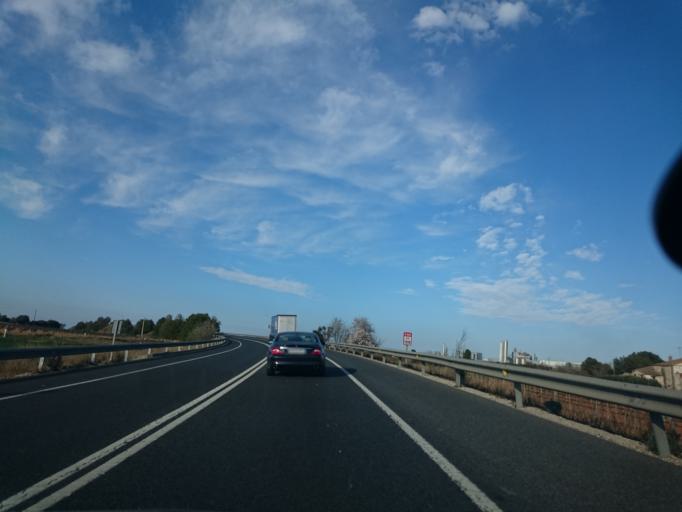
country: ES
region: Catalonia
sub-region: Provincia de Barcelona
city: Castellet
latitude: 41.3199
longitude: 1.6435
